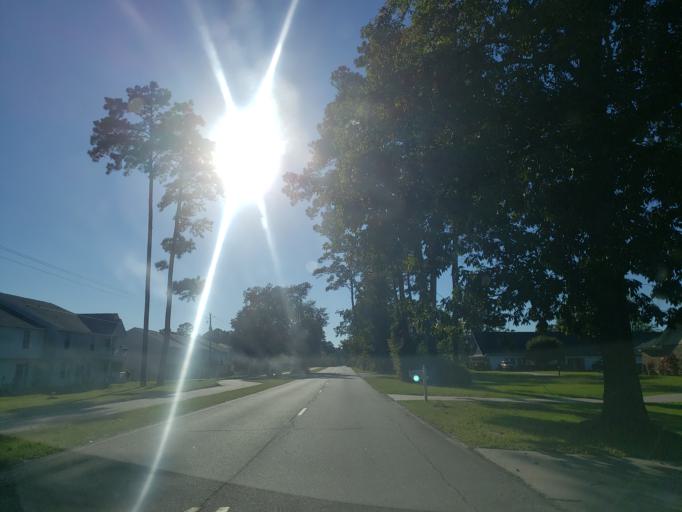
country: US
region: Georgia
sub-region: Chatham County
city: Georgetown
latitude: 31.9954
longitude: -81.2743
